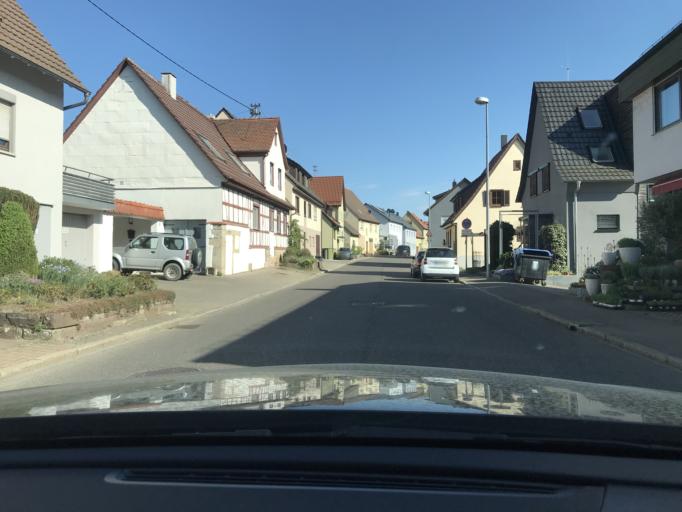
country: DE
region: Baden-Wuerttemberg
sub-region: Regierungsbezirk Stuttgart
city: Weinstadt-Endersbach
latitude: 48.7927
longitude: 9.4003
